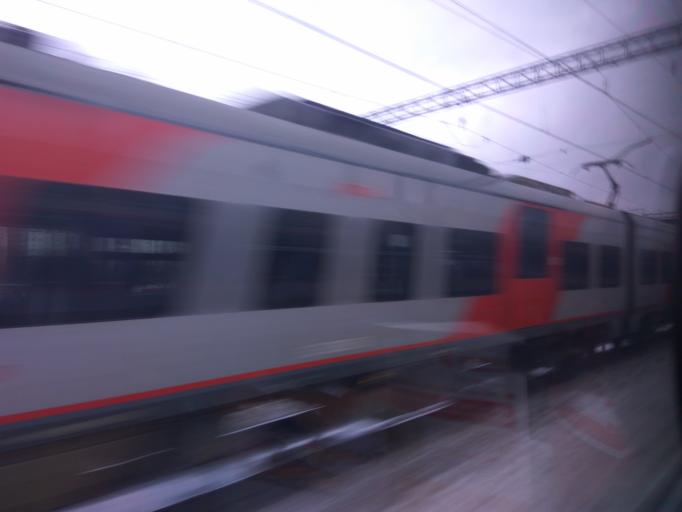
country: RU
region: Moscow
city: Zelenograd
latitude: 55.9880
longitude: 37.1637
